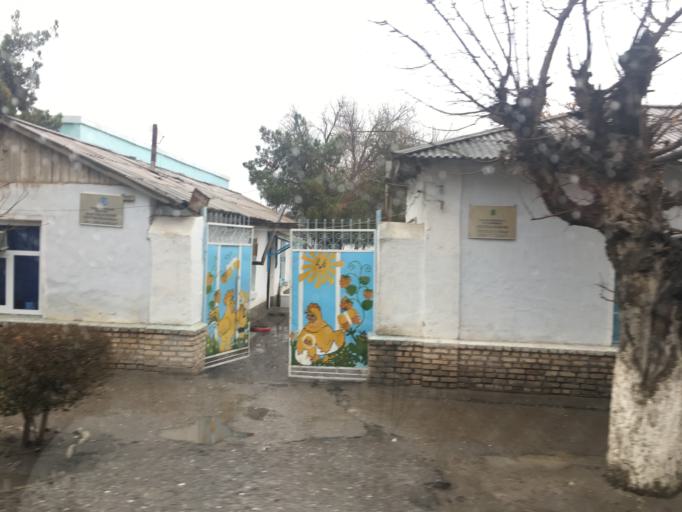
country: TM
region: Mary
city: Yoloeten
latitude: 37.3027
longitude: 62.3570
